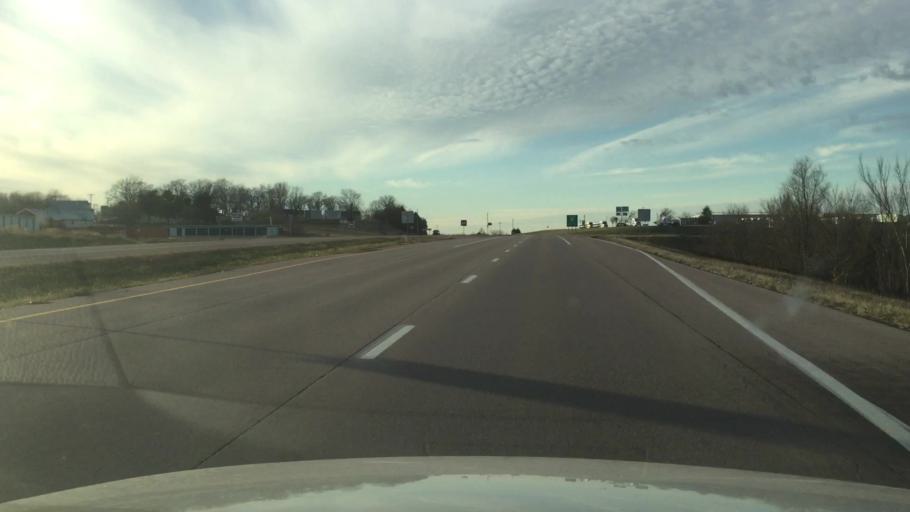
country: US
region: Missouri
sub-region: Miller County
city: Eldon
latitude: 38.3692
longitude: -92.5212
